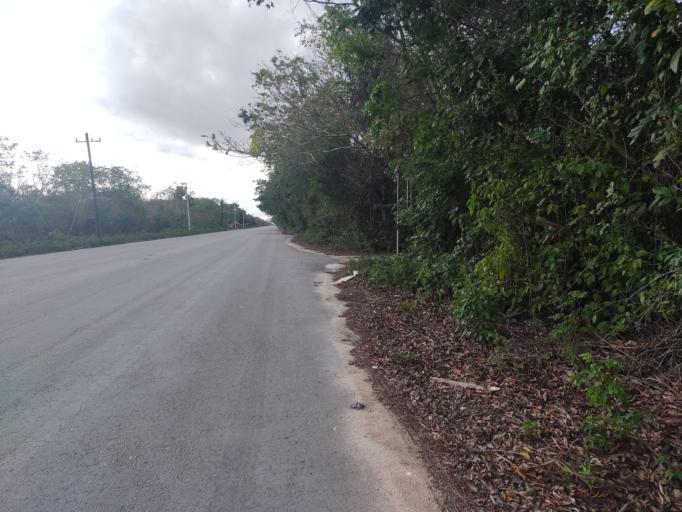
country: MX
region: Quintana Roo
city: San Miguel de Cozumel
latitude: 20.4427
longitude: -86.8661
